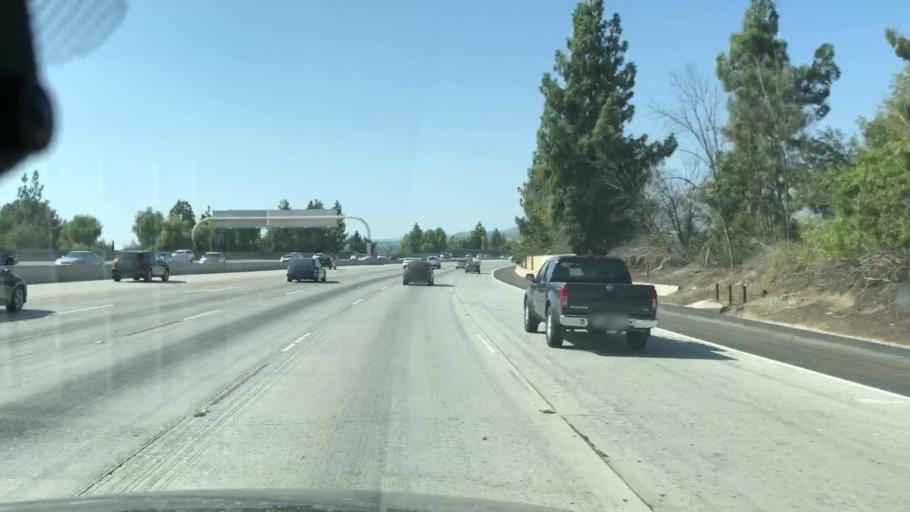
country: US
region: California
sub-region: Los Angeles County
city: San Fernando
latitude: 34.2667
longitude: -118.4818
